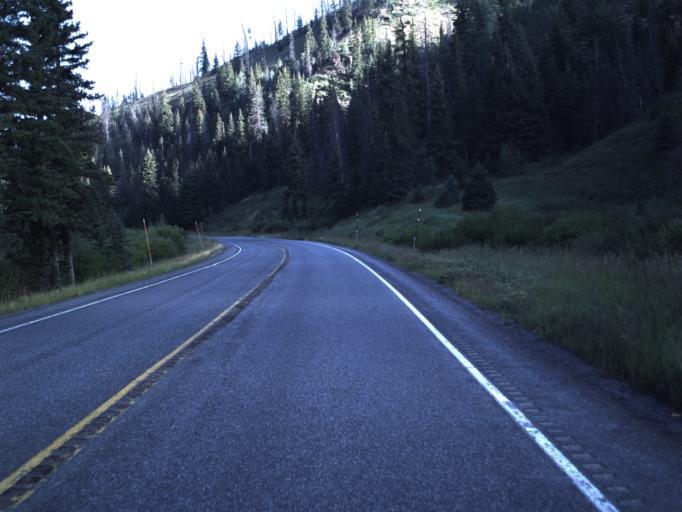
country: US
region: Utah
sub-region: Sanpete County
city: Fairview
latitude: 39.5784
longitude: -111.1855
